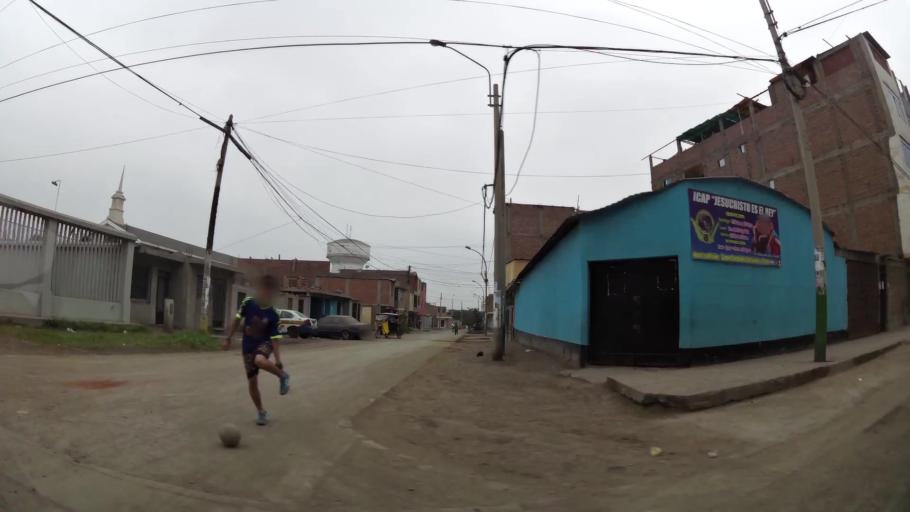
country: PE
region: Lima
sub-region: Lima
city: Urb. Santo Domingo
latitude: -11.9071
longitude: -77.0418
